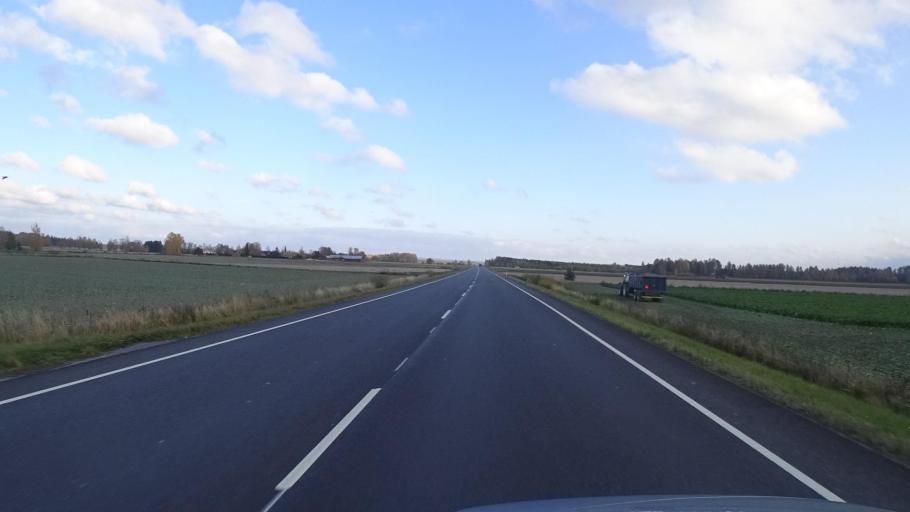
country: FI
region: Satakunta
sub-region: Rauma
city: Koeylioe
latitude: 61.0775
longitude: 22.2847
